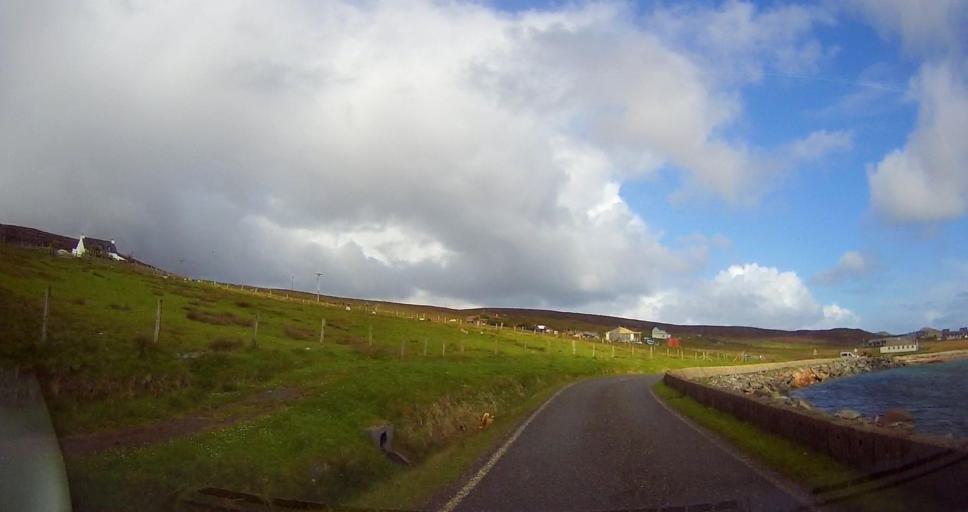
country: GB
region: Scotland
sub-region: Shetland Islands
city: Lerwick
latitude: 60.5819
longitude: -1.3347
